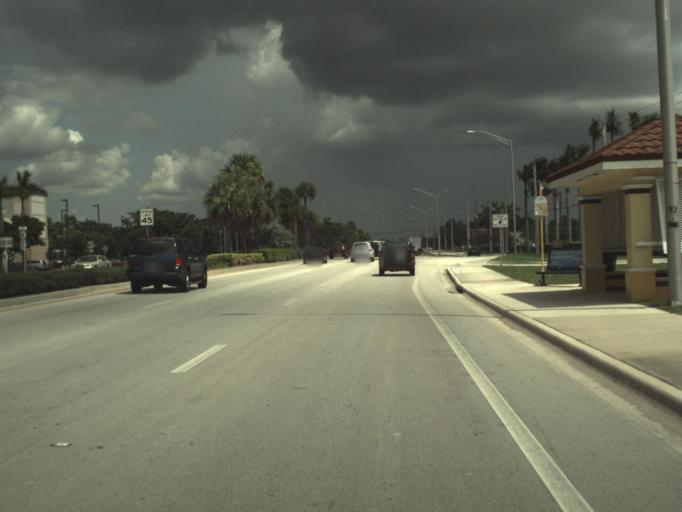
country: US
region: Florida
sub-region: Broward County
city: Margate
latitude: 26.2620
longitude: -80.2015
